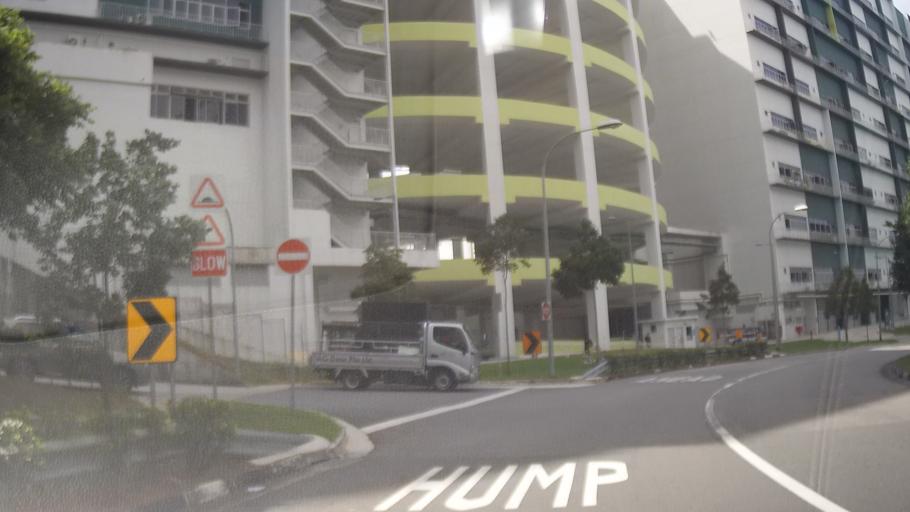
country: MY
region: Johor
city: Johor Bahru
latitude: 1.4094
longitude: 103.7579
